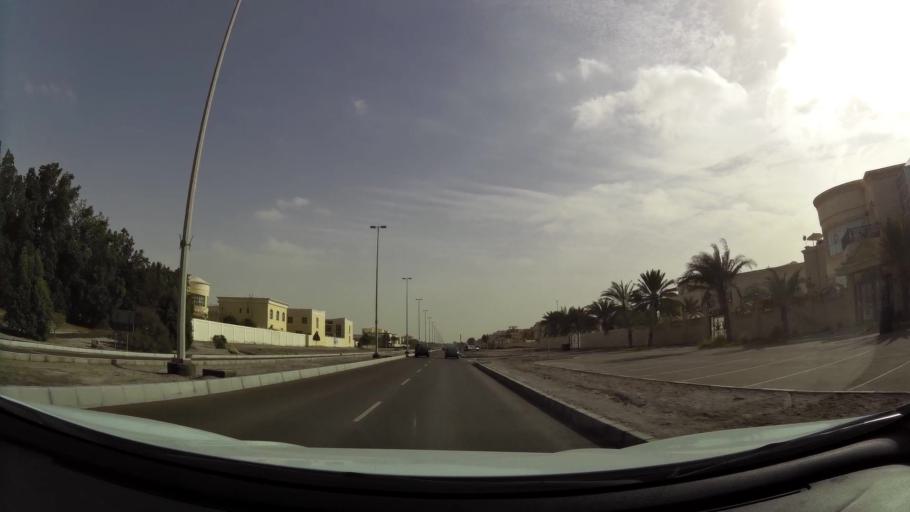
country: AE
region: Abu Dhabi
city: Abu Dhabi
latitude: 24.4135
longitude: 54.6028
